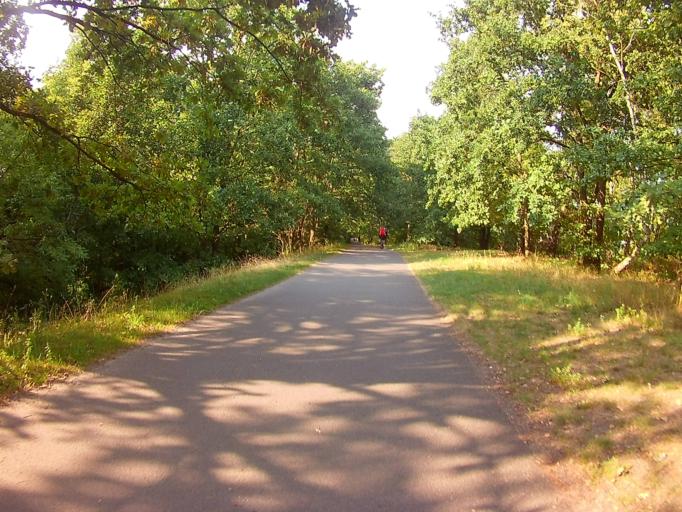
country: DE
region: Berlin
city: Kopenick Bezirk
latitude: 52.4698
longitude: 13.5670
